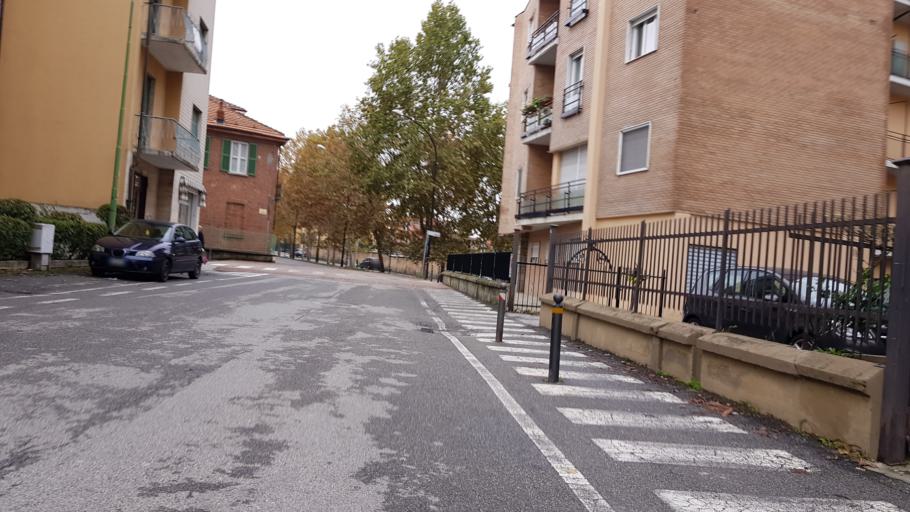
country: IT
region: Piedmont
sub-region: Provincia di Cuneo
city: Fossano
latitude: 44.5546
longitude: 7.7309
